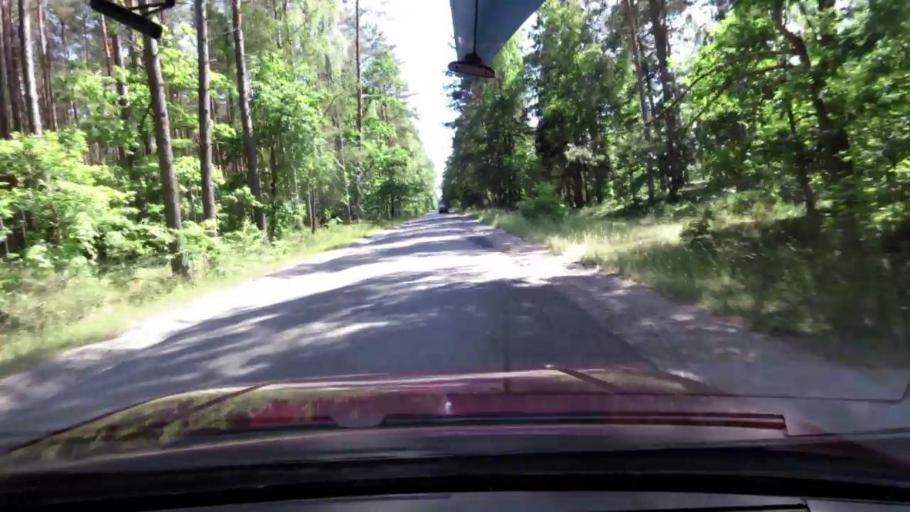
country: PL
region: Pomeranian Voivodeship
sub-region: Powiat slupski
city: Kepice
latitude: 54.3198
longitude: 16.9620
